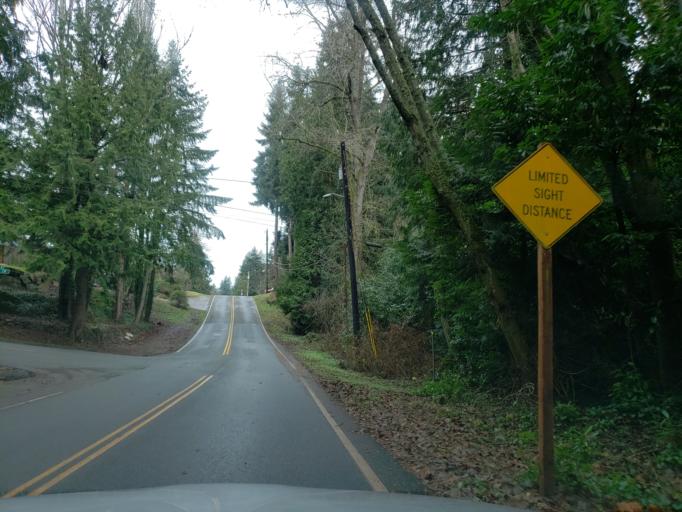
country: US
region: Washington
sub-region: Snohomish County
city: Meadowdale
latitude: 47.8321
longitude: -122.3413
